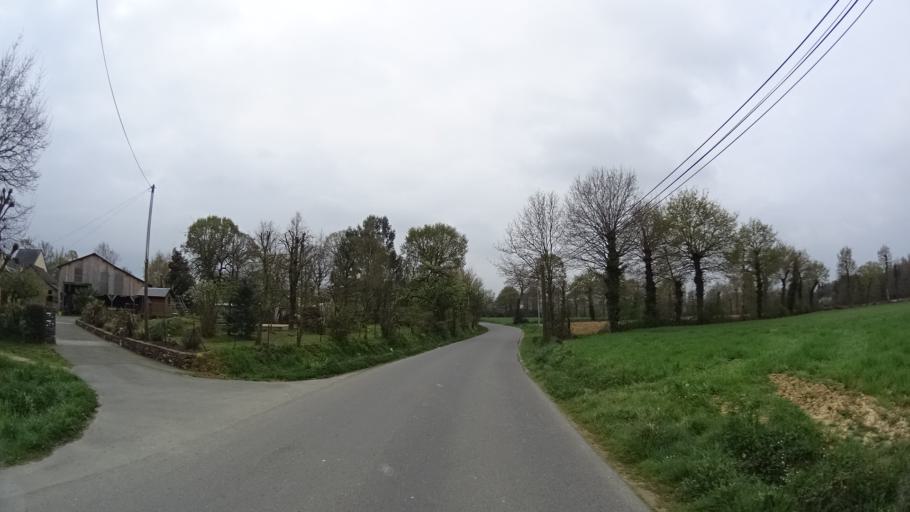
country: FR
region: Brittany
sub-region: Departement d'Ille-et-Vilaine
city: Saint-Gilles
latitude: 48.1519
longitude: -1.8420
